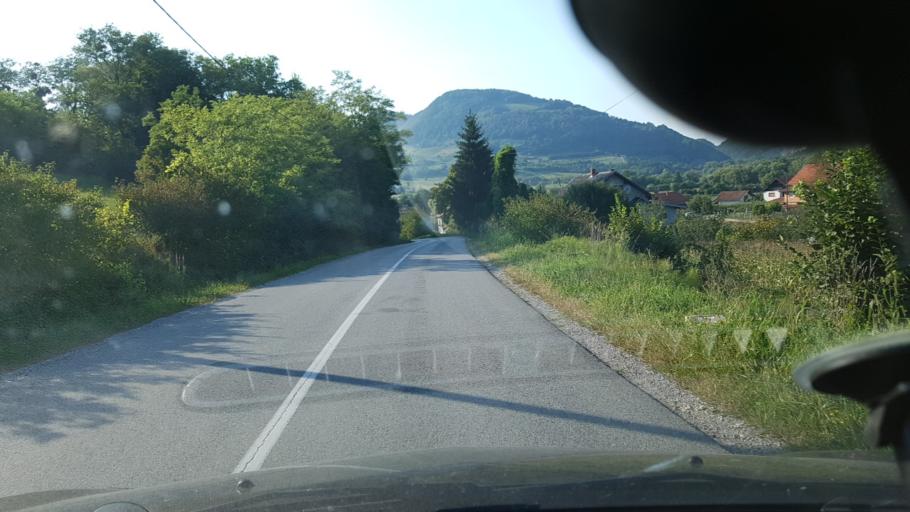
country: SI
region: Bistrica ob Sotli
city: Bistrica ob Sotli
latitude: 46.0354
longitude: 15.7327
